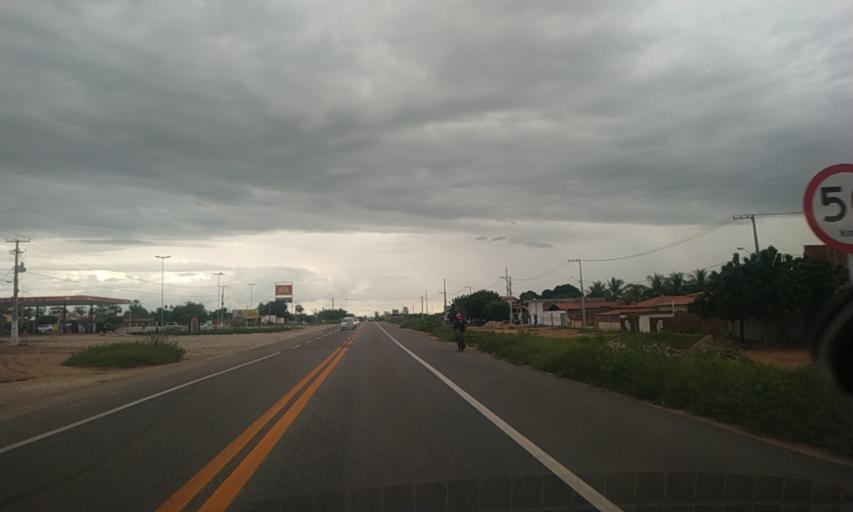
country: BR
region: Rio Grande do Norte
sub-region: Mossoro
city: Mossoro
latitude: -5.1918
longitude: -37.3101
